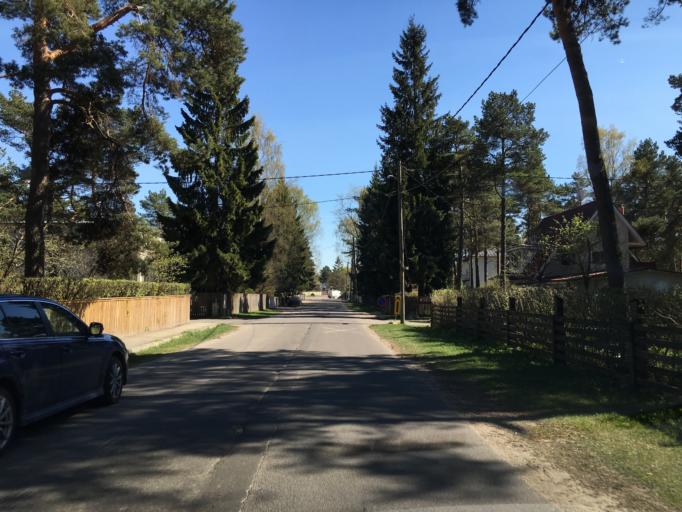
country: EE
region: Harju
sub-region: Tallinna linn
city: Tallinn
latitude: 59.3877
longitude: 24.7122
